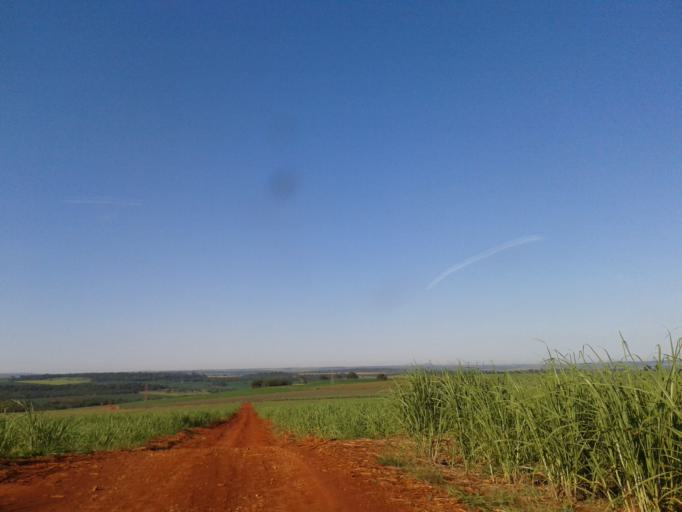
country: BR
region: Minas Gerais
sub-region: Centralina
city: Centralina
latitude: -18.6694
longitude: -49.2668
